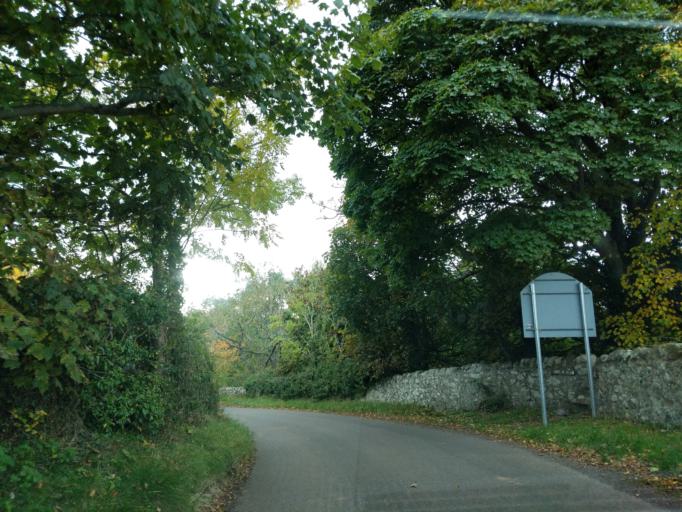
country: GB
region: Scotland
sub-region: East Lothian
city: East Linton
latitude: 55.9407
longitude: -2.7083
